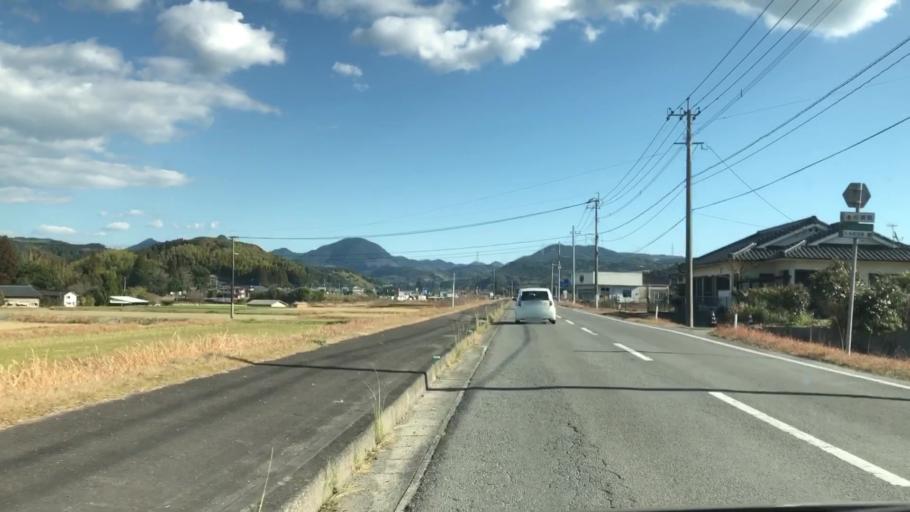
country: JP
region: Kagoshima
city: Satsumasendai
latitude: 31.7970
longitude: 130.4356
